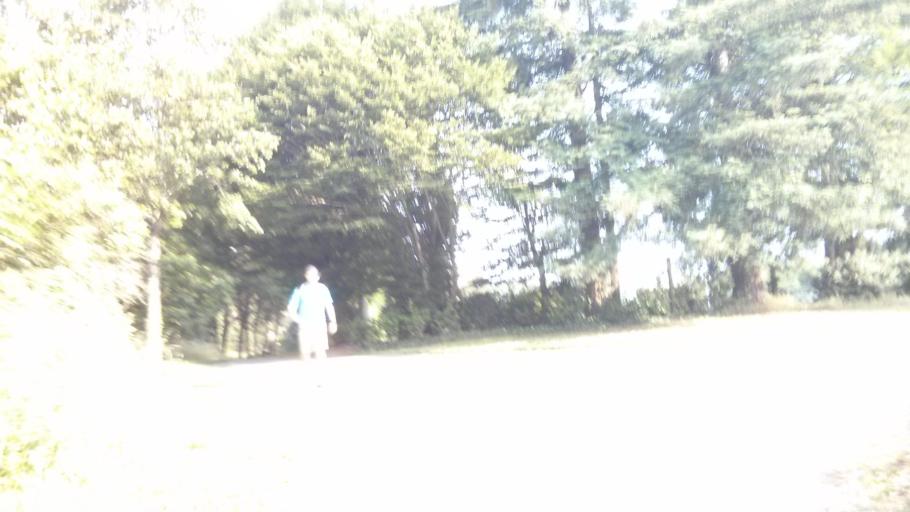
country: FR
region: Pays de la Loire
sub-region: Departement de la Loire-Atlantique
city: Reze
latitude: 47.1833
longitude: -1.5309
